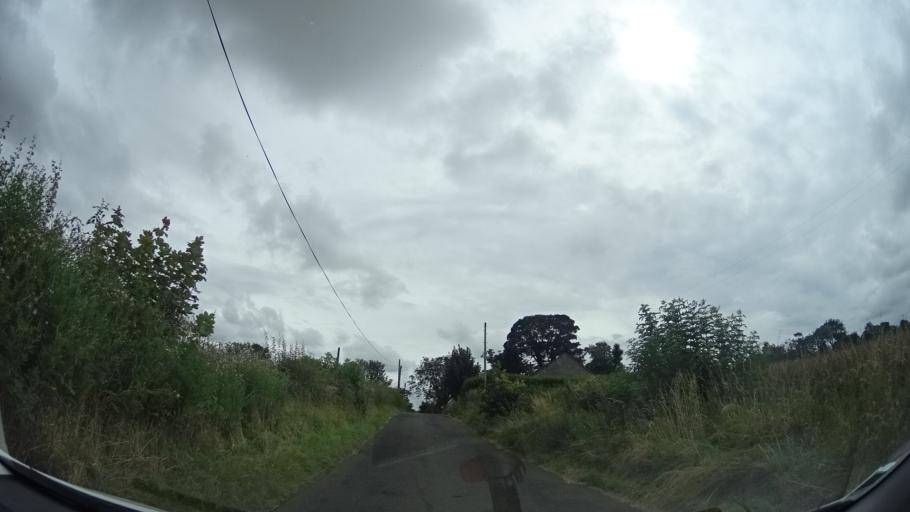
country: GB
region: Scotland
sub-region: Edinburgh
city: Newbridge
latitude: 55.9231
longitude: -3.4208
